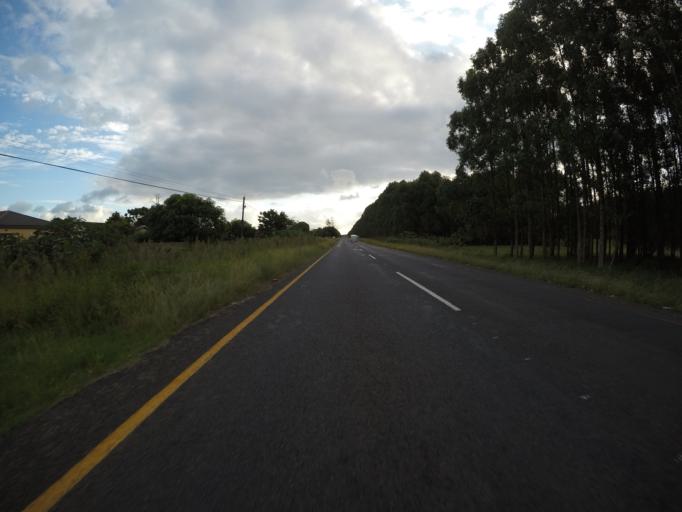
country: ZA
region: KwaZulu-Natal
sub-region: uMkhanyakude District Municipality
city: Mtubatuba
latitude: -28.3965
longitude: 32.2167
